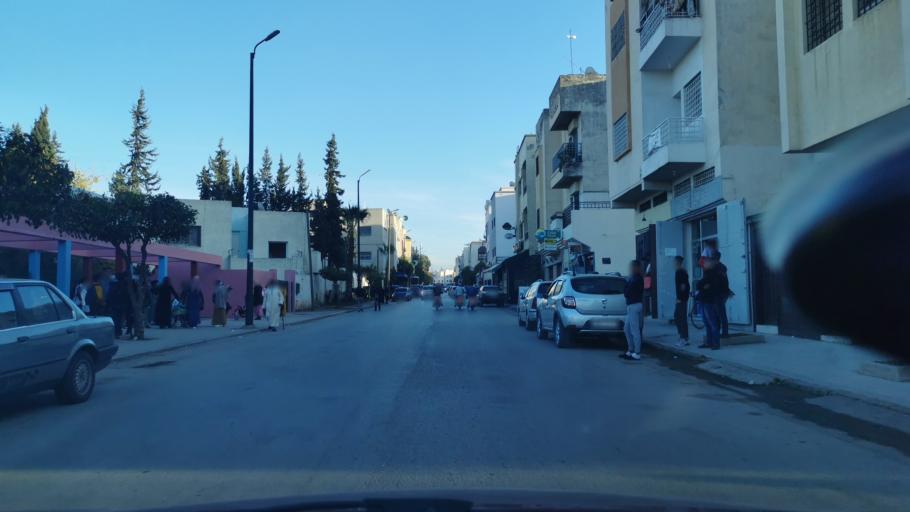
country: MA
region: Fes-Boulemane
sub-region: Fes
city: Fes
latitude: 34.0199
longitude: -4.9775
